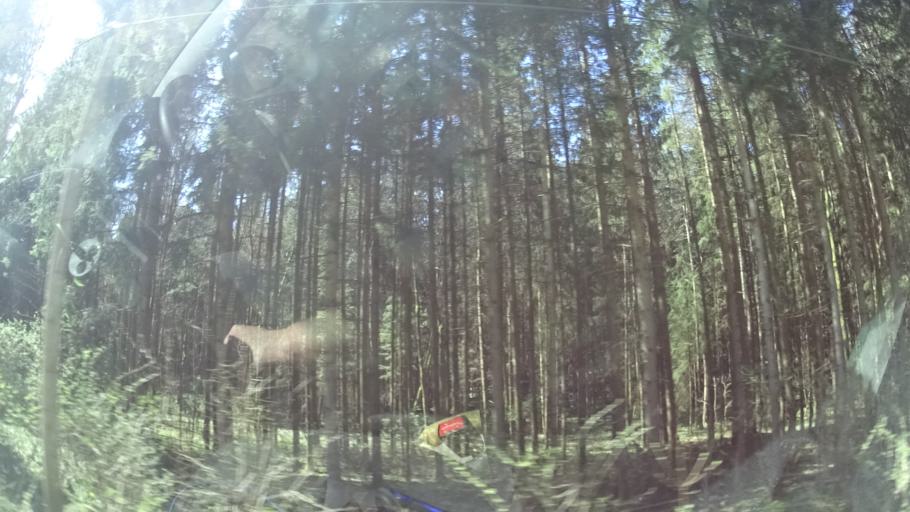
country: DE
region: Bavaria
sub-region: Upper Palatinate
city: Kastl
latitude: 49.3870
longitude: 11.6862
